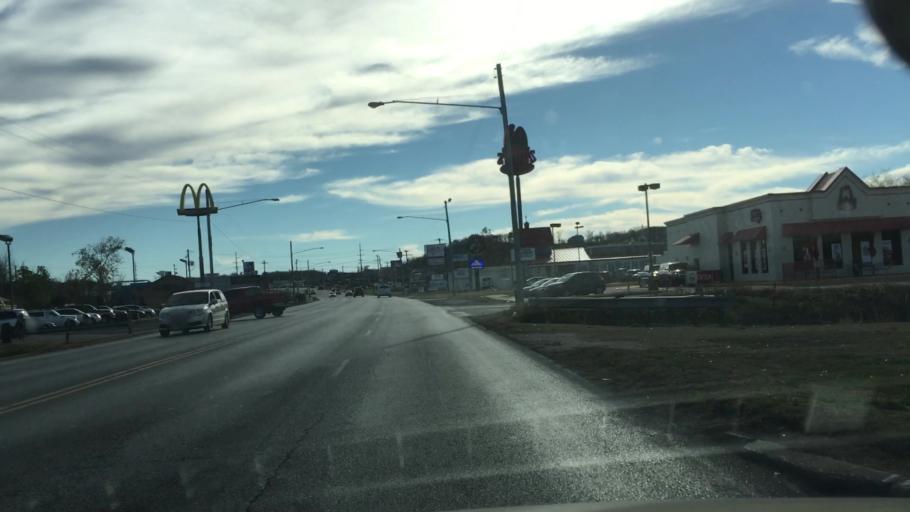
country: US
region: Oklahoma
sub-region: Cherokee County
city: Tahlequah
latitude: 35.8978
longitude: -94.9761
